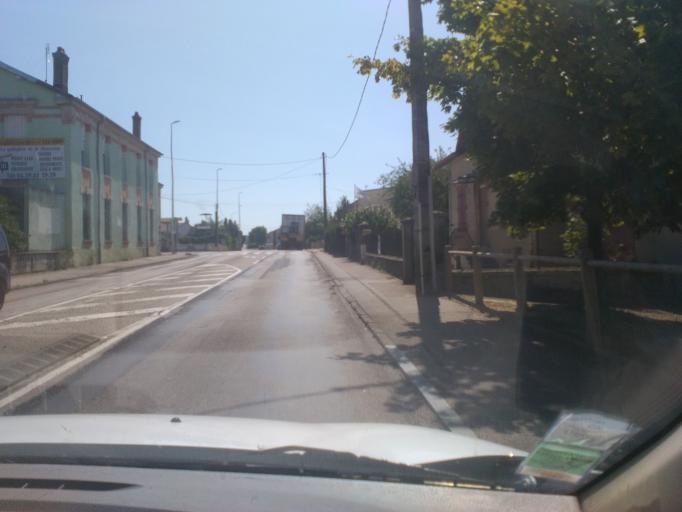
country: FR
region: Lorraine
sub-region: Departement des Vosges
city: Rambervillers
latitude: 48.3349
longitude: 6.6359
